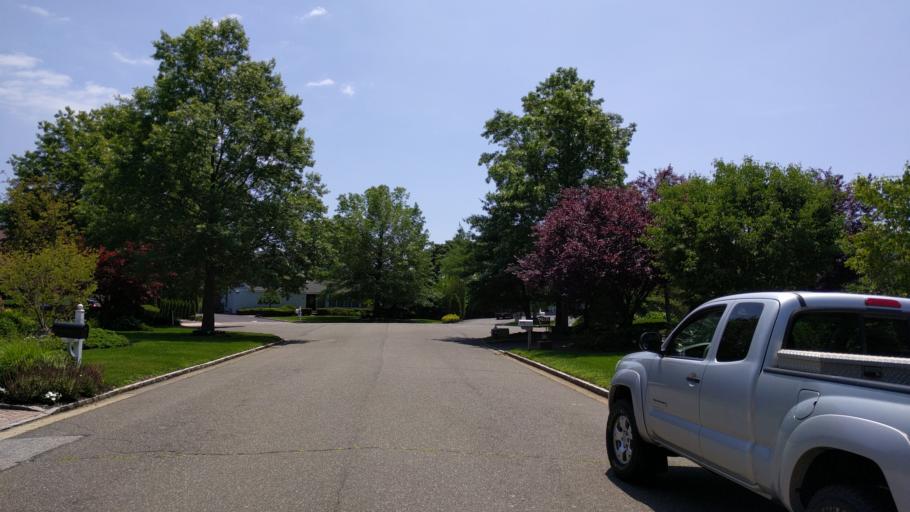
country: US
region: New York
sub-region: Nassau County
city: Syosset
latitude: 40.8209
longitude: -73.5101
